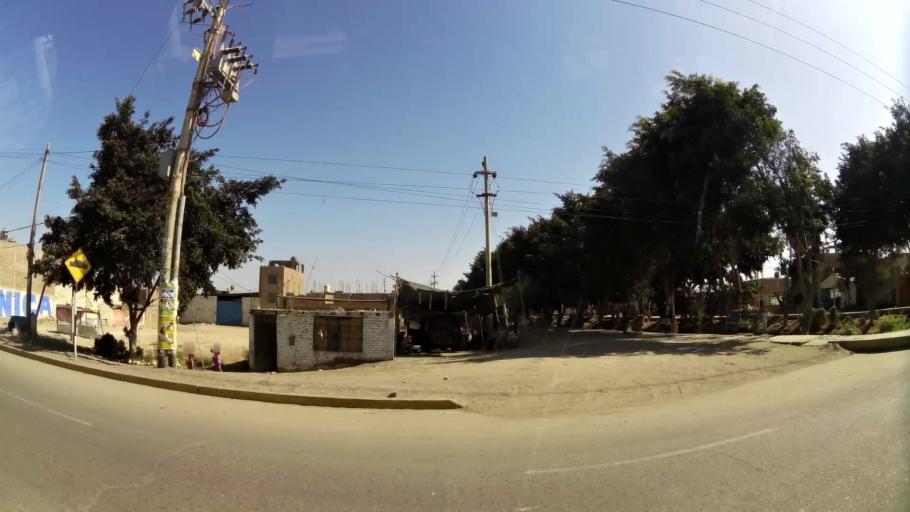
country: PE
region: Ica
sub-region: Provincia de Ica
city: La Tinguina
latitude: -14.0520
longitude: -75.7045
